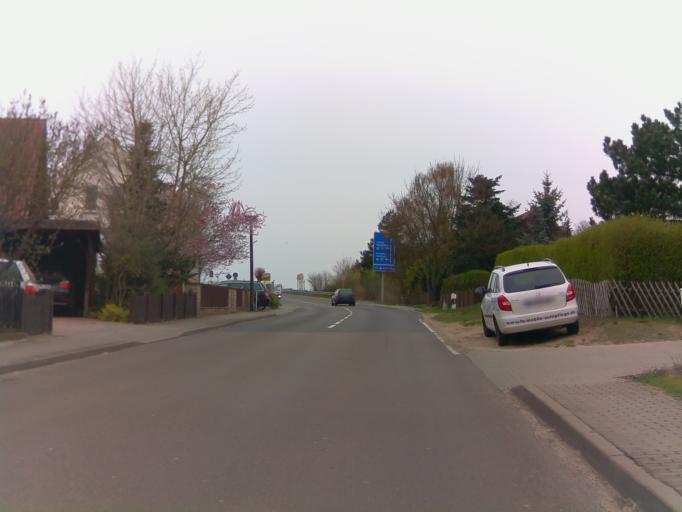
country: DE
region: Brandenburg
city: Werder
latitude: 52.4343
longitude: 12.9336
